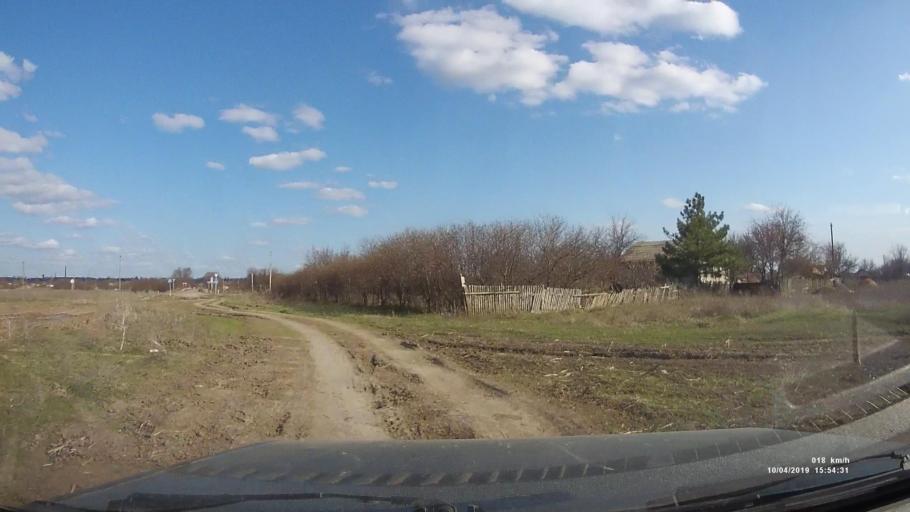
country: RU
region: Rostov
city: Masalovka
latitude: 48.4141
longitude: 40.2602
